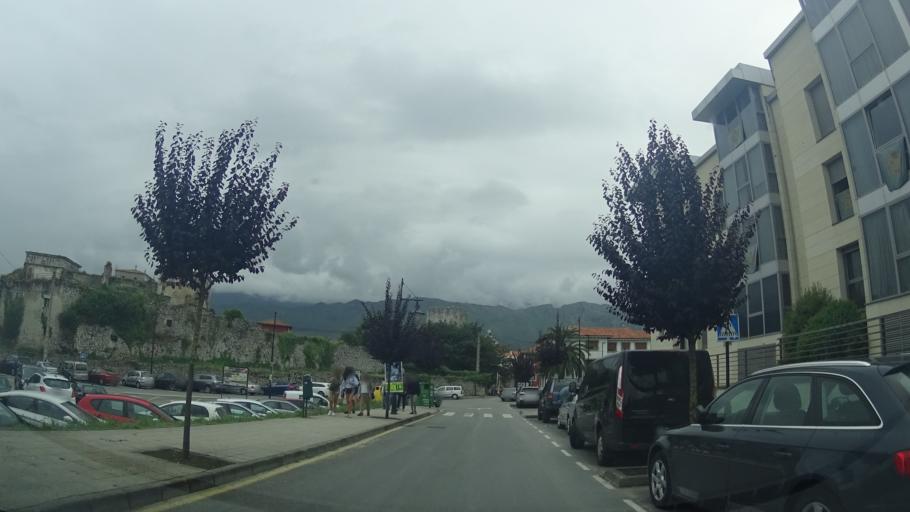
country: ES
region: Asturias
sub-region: Province of Asturias
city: Llanes
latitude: 43.4225
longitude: -4.7549
